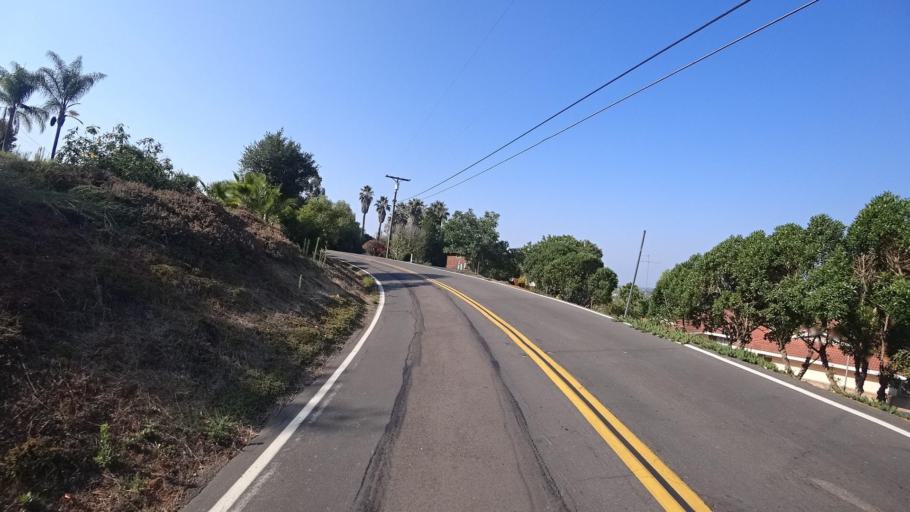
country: US
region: California
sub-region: San Diego County
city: Vista
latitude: 33.2299
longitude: -117.2190
